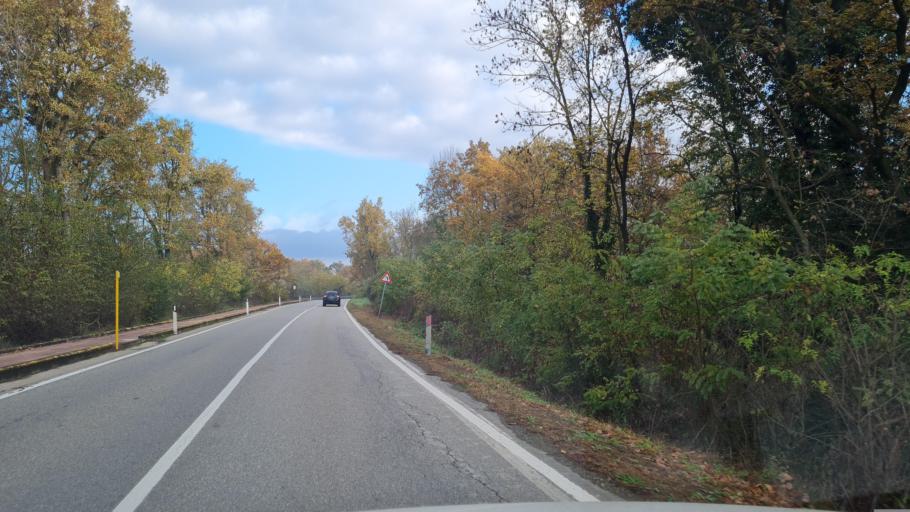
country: IT
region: Piedmont
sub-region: Provincia di Biella
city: Castelletto Cervo
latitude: 45.5236
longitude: 8.2233
